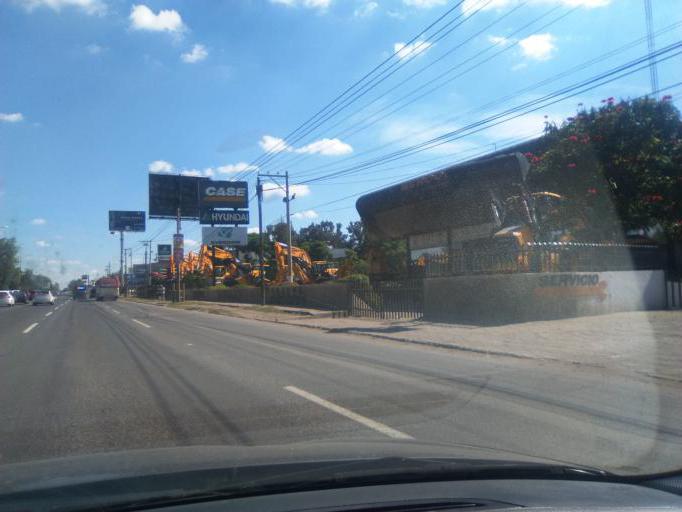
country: MX
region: Guanajuato
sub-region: Leon
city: Fraccionamiento Paraiso Real
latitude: 21.0817
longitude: -101.6102
